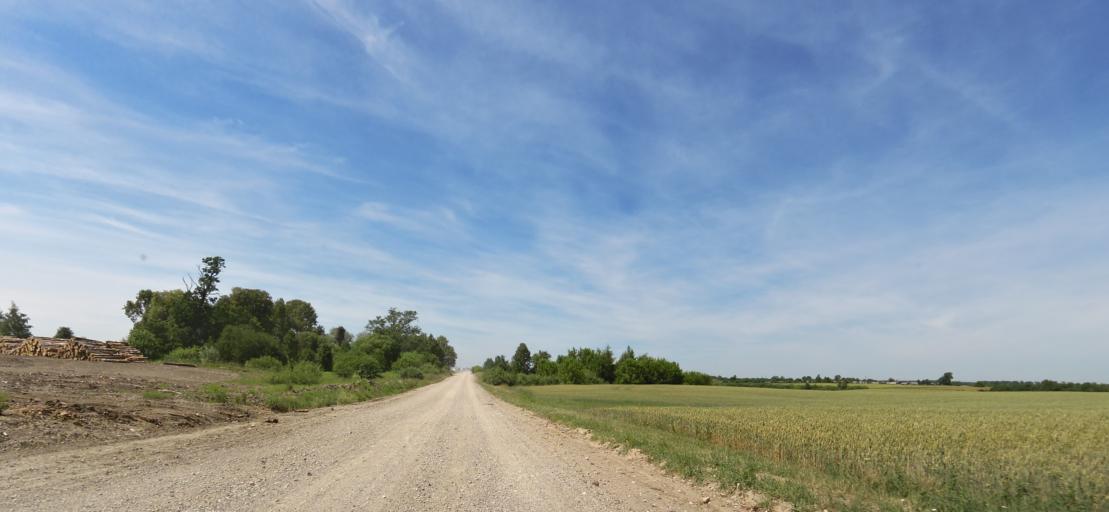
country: LT
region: Vilnius County
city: Ukmerge
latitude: 55.3022
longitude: 24.8067
